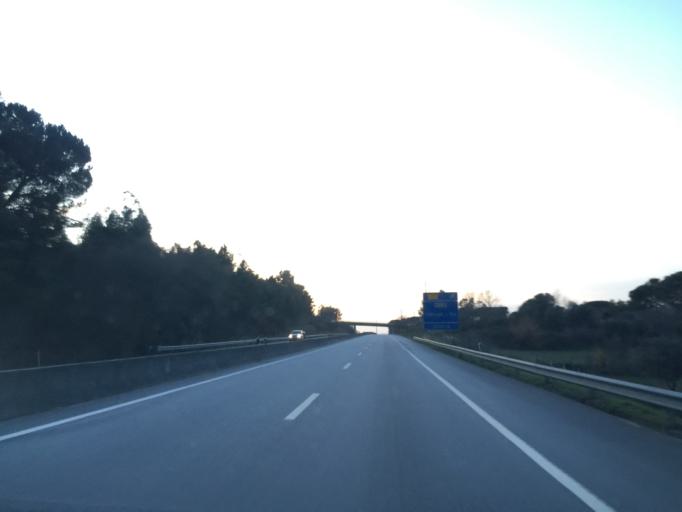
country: PT
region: Viseu
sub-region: Concelho de Carregal do Sal
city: Carregal do Sal
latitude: 40.4389
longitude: -7.9971
